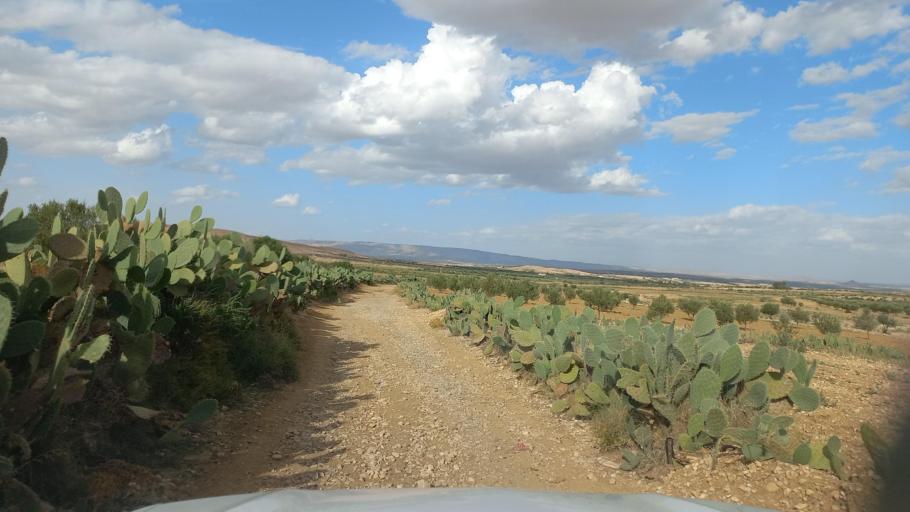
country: TN
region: Al Qasrayn
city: Sbiba
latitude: 35.4523
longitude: 9.0904
